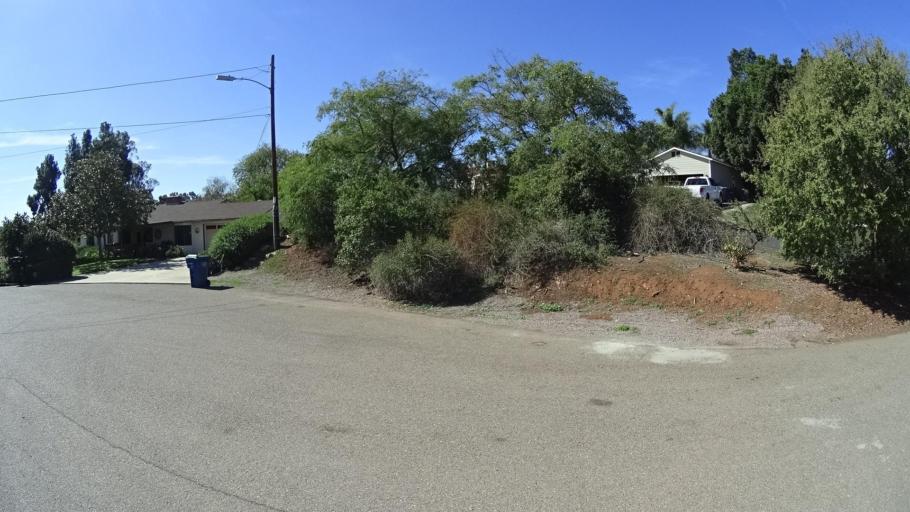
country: US
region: California
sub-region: San Diego County
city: Casa de Oro-Mount Helix
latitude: 32.7536
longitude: -116.9629
